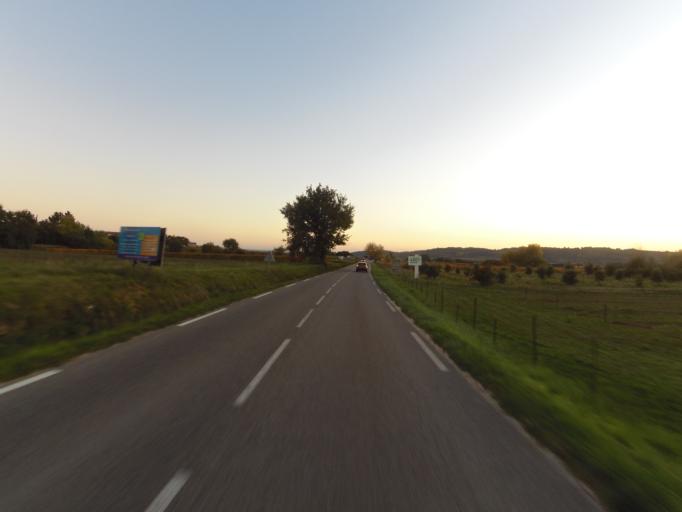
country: FR
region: Provence-Alpes-Cote d'Azur
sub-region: Departement du Vaucluse
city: Bedoin
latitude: 44.1121
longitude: 5.1771
